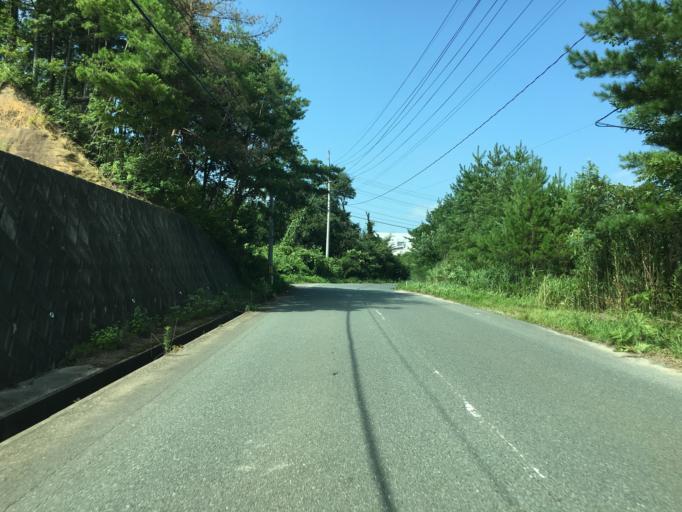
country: JP
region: Miyagi
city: Marumori
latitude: 37.8968
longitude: 140.8898
